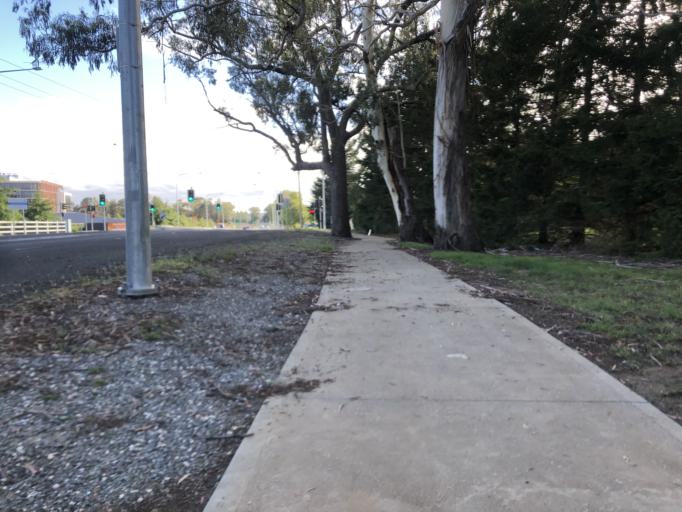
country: AU
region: New South Wales
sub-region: Orange Municipality
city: Orange
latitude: -33.3185
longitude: 149.0894
